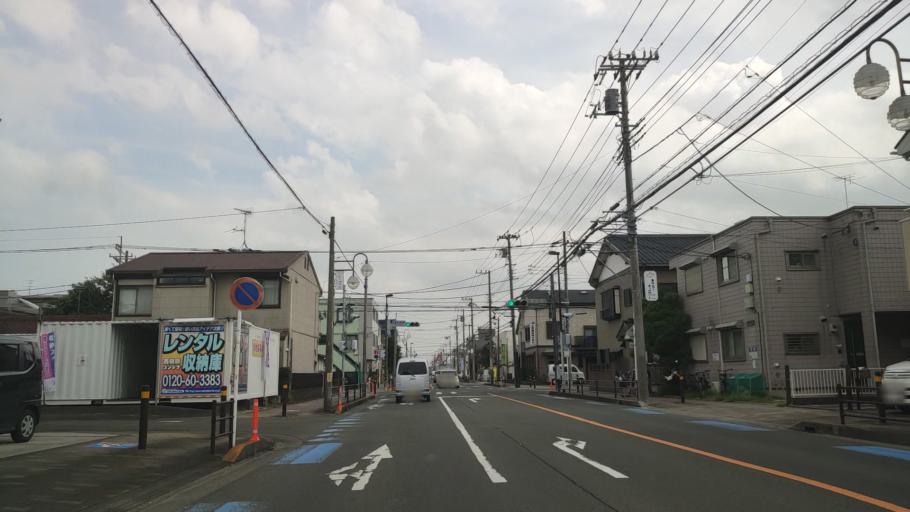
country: JP
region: Kanagawa
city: Minami-rinkan
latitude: 35.4852
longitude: 139.4500
